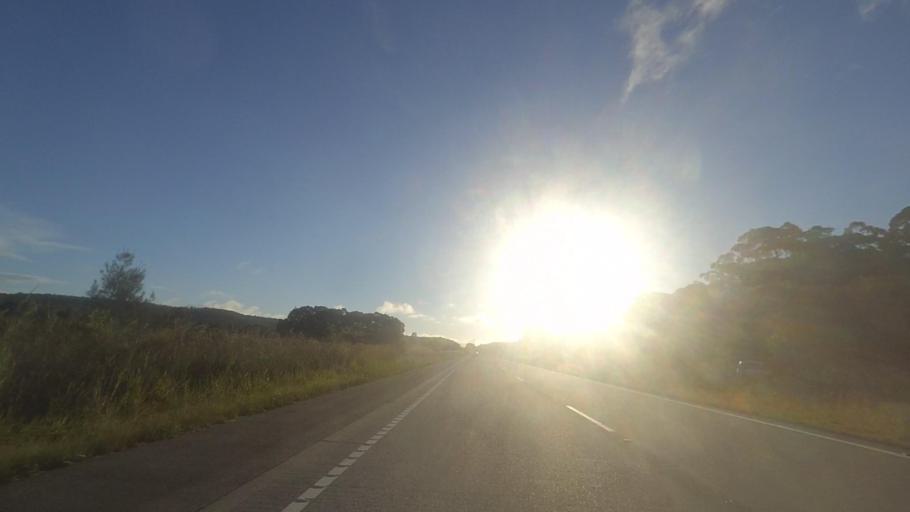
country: AU
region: New South Wales
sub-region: Great Lakes
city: Bulahdelah
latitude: -32.5249
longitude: 152.1965
